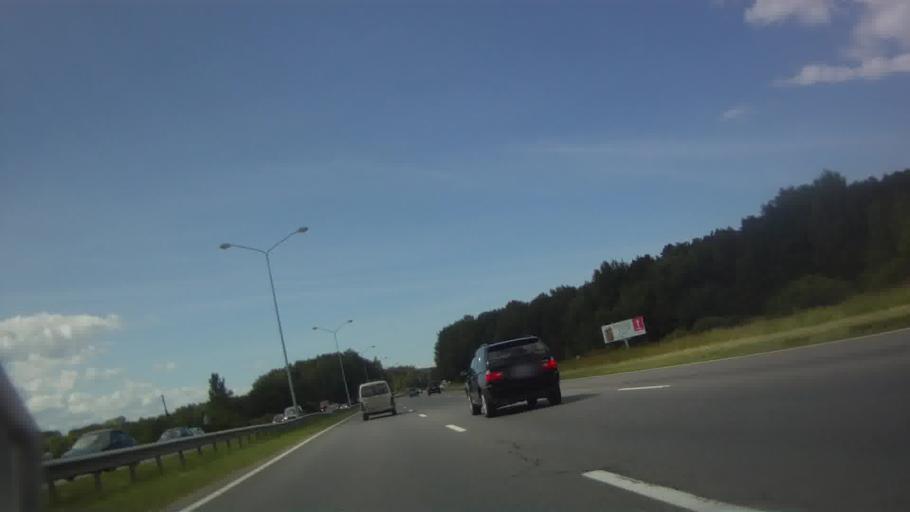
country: LV
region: Babite
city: Pinki
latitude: 56.9628
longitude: 23.8808
